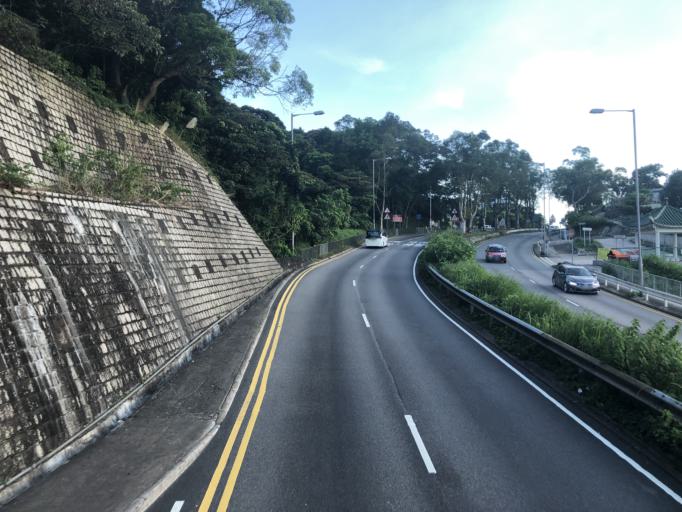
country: HK
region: Sai Kung
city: Sai Kung
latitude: 22.3414
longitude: 114.2484
